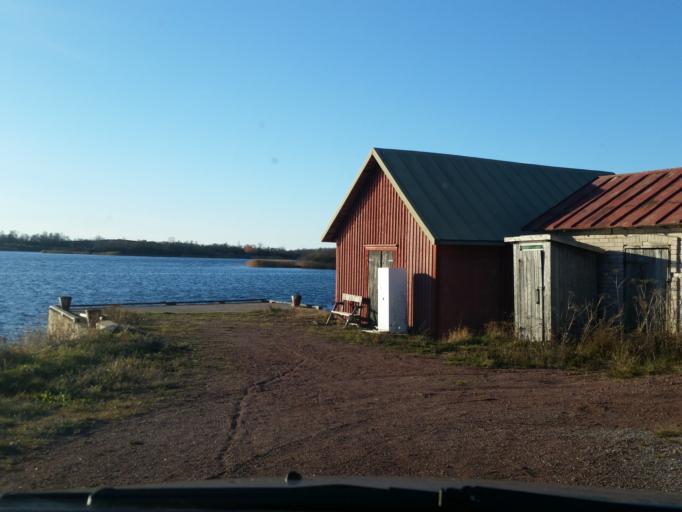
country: AX
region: Alands skaergard
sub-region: Braendoe
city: Braendoe
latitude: 60.4120
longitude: 21.0367
